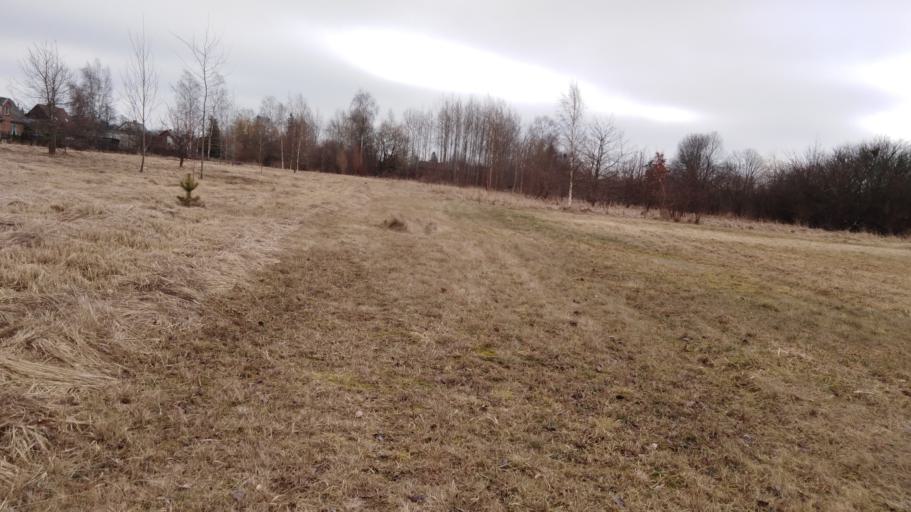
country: LV
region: Kuldigas Rajons
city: Kuldiga
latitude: 56.9739
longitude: 21.9832
